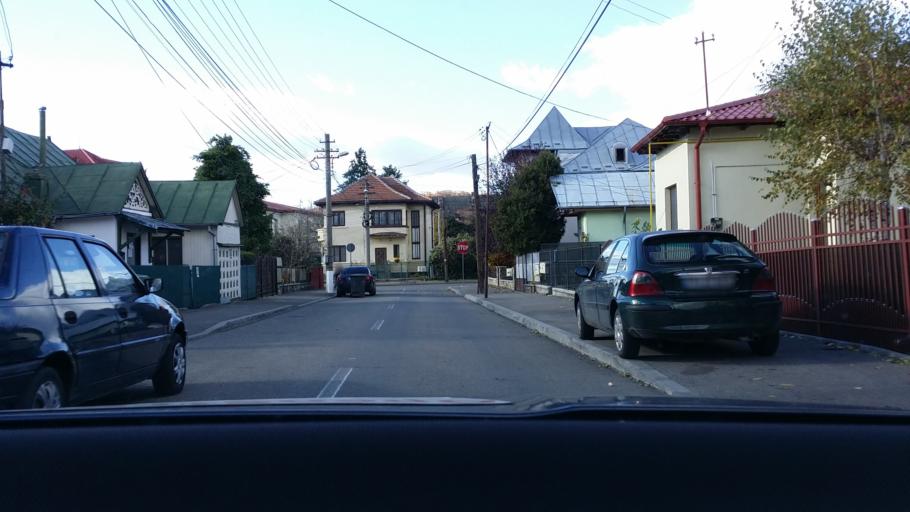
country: RO
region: Prahova
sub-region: Municipiul Campina
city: Campina
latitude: 45.1237
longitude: 25.7316
